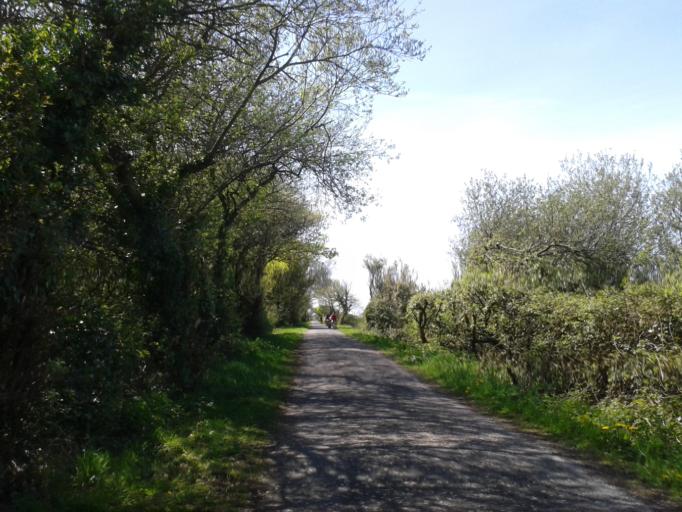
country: GB
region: England
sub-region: Devon
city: Fremington
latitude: 51.0764
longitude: -4.1339
